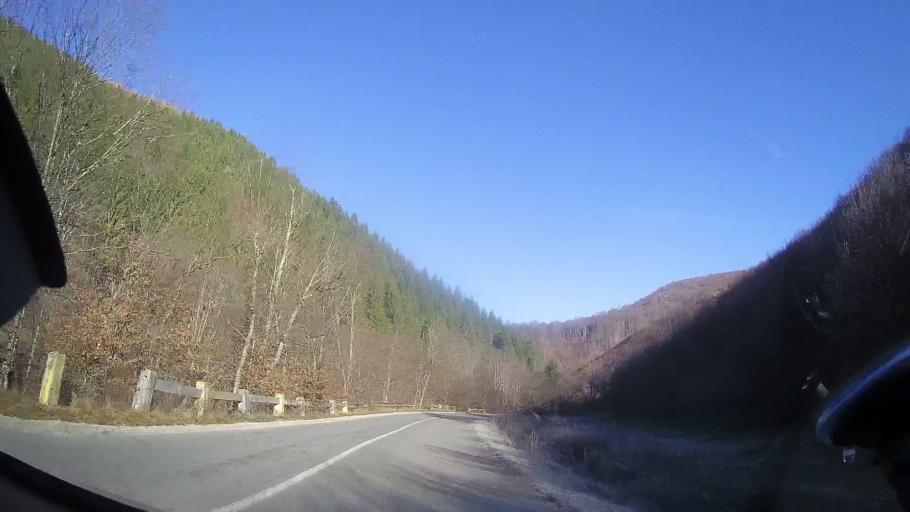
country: RO
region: Cluj
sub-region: Comuna Sacueu
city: Sacuieu
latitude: 46.8360
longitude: 22.8597
